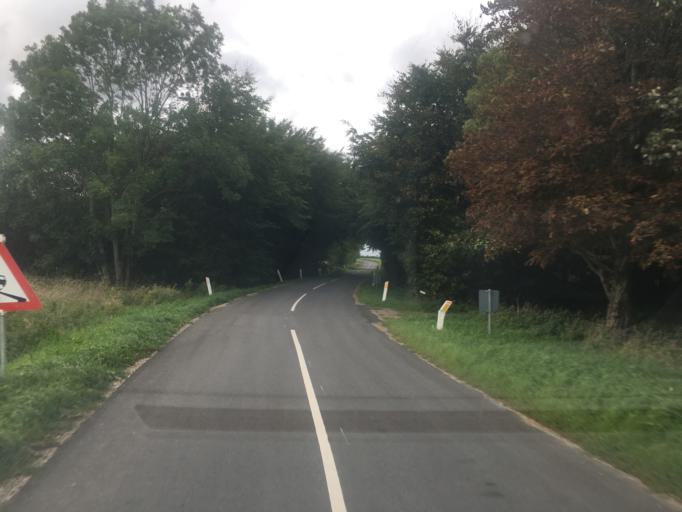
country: DE
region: Schleswig-Holstein
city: Aventoft
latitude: 54.9605
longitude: 8.8033
